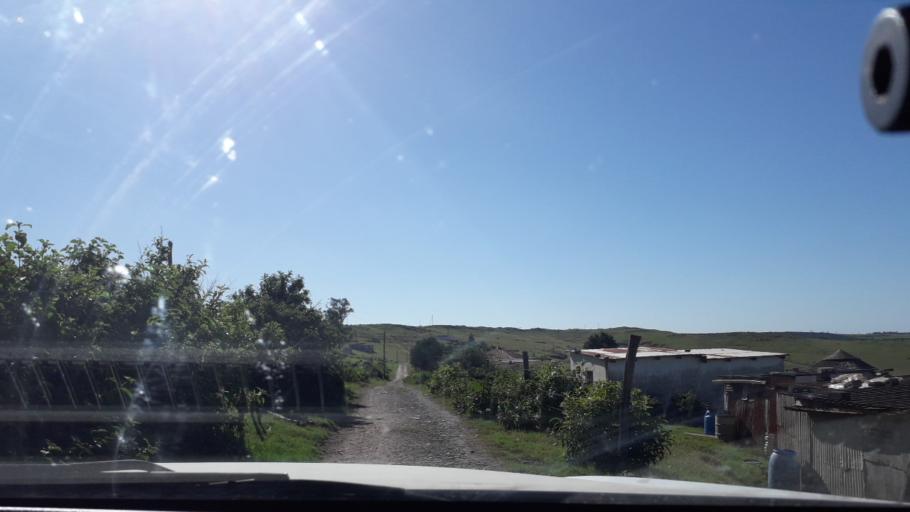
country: ZA
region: Eastern Cape
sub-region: Buffalo City Metropolitan Municipality
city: East London
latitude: -32.8435
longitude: 27.9917
